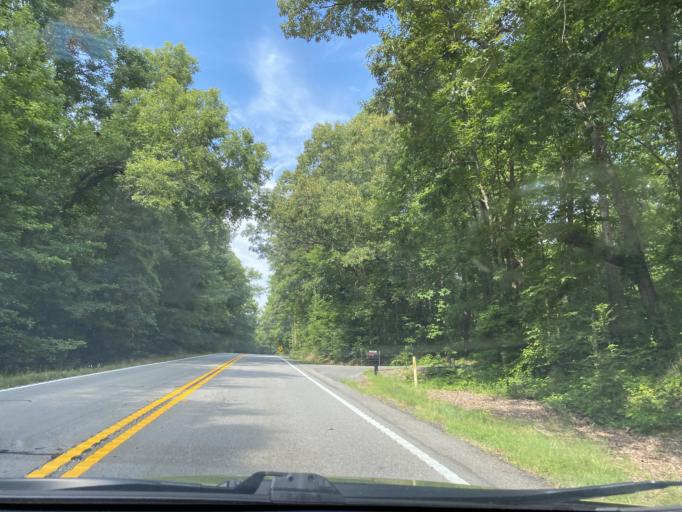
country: US
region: Georgia
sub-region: Coweta County
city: East Newnan
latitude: 33.2740
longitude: -84.7049
